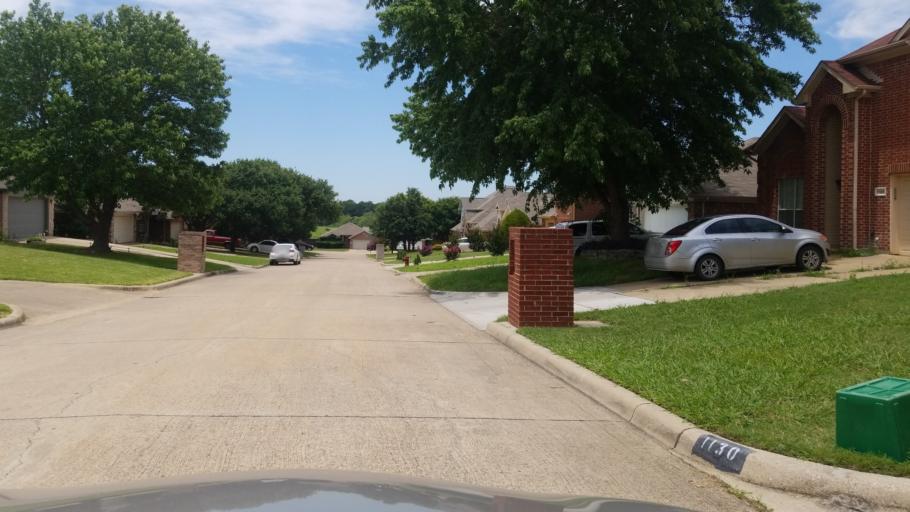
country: US
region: Texas
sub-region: Dallas County
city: Grand Prairie
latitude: 32.6781
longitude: -96.9913
